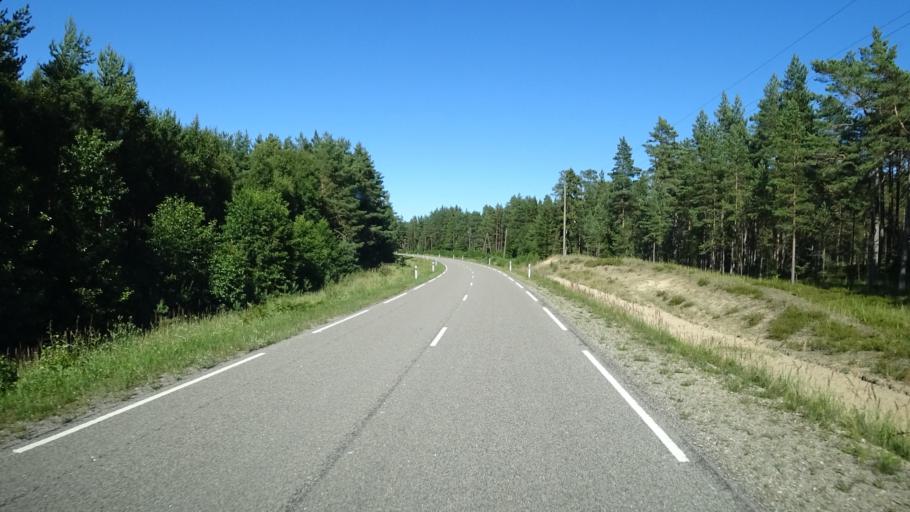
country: LV
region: Dundaga
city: Dundaga
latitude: 57.6824
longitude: 22.3624
